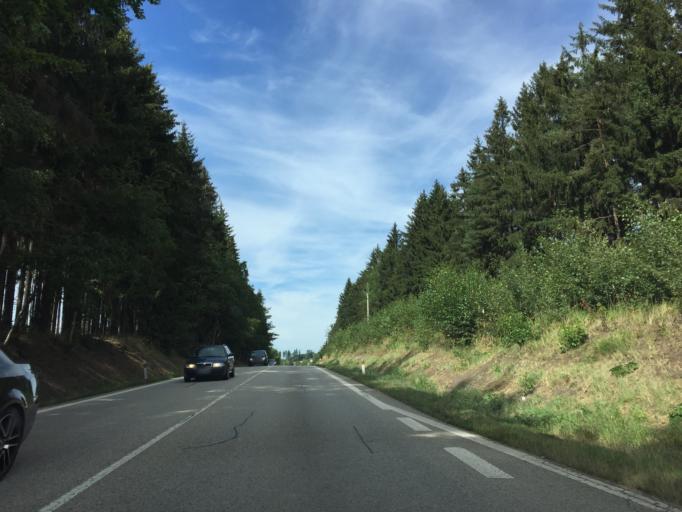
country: CZ
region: Central Bohemia
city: Votice
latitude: 49.5902
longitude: 14.6615
